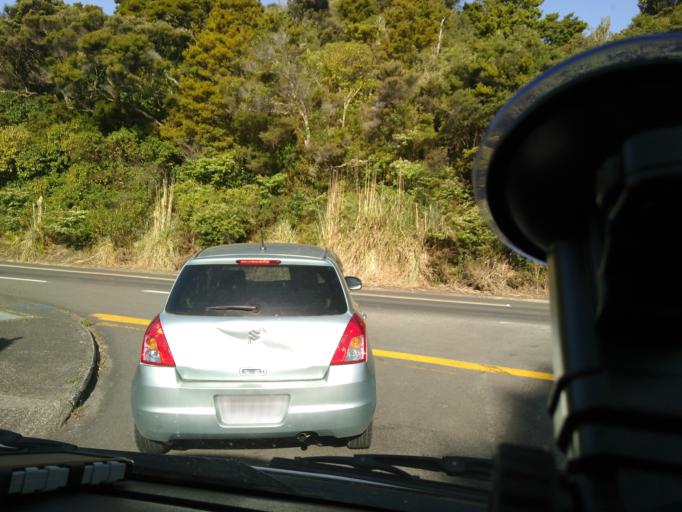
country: NZ
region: Northland
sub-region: Far North District
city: Paihia
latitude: -35.2870
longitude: 174.0960
